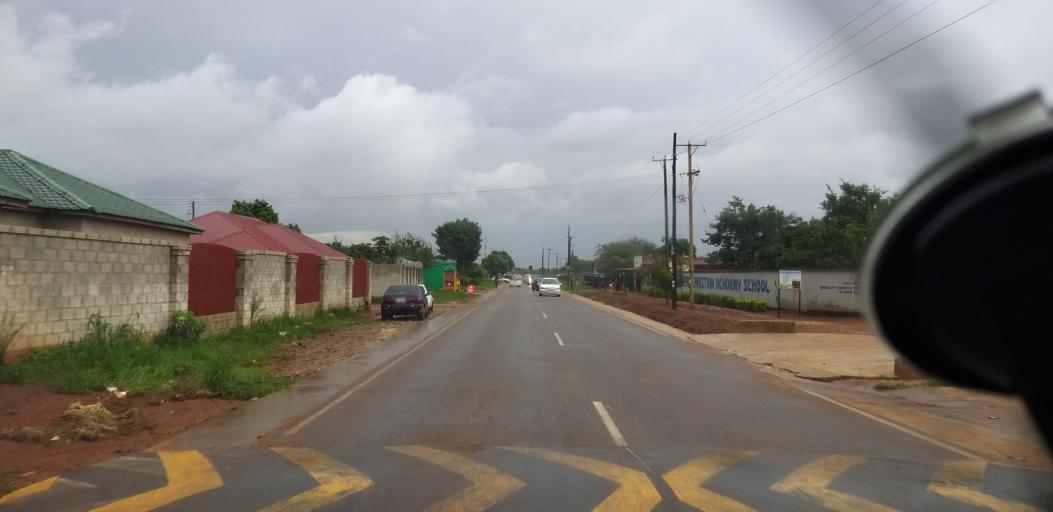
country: ZM
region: Lusaka
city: Lusaka
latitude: -15.4982
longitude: 28.3126
